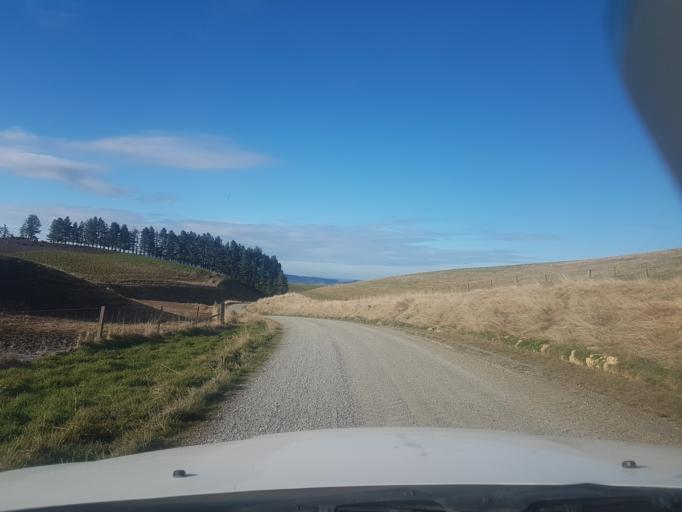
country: NZ
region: Canterbury
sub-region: Timaru District
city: Pleasant Point
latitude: -44.1665
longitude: 170.8945
